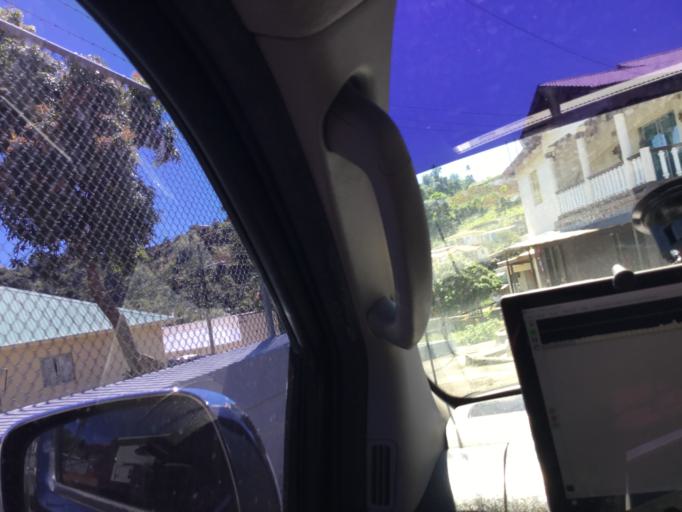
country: VC
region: Charlotte
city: Byera Village
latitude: 13.2470
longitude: -61.1414
